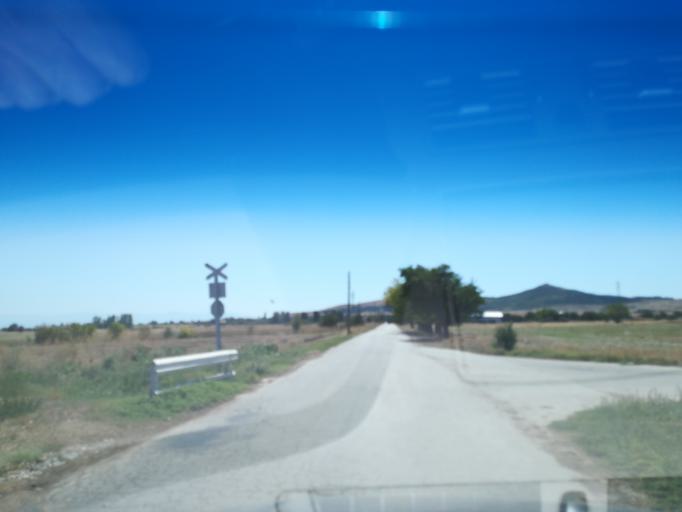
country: BG
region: Pazardzhik
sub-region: Obshtina Pazardzhik
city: Pazardzhik
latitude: 42.3471
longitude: 24.4011
